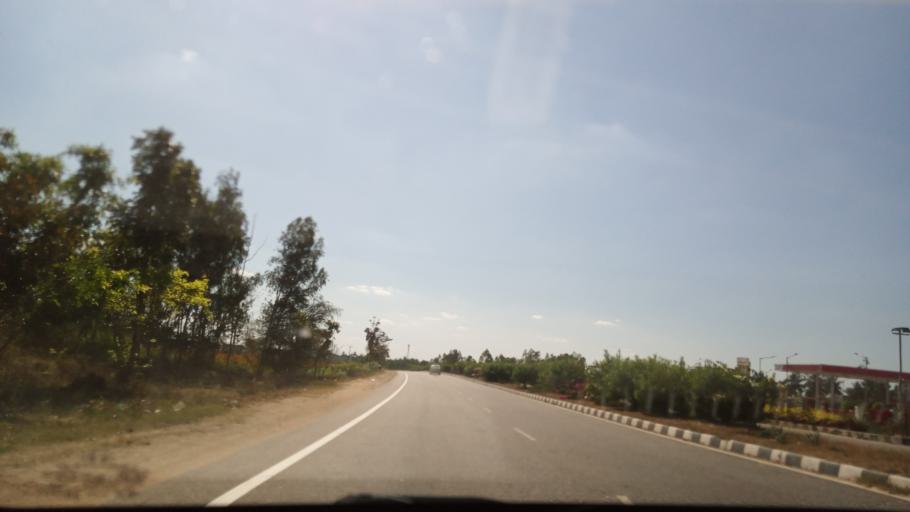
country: IN
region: Karnataka
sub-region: Kolar
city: Mulbagal
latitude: 13.2012
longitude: 78.4891
